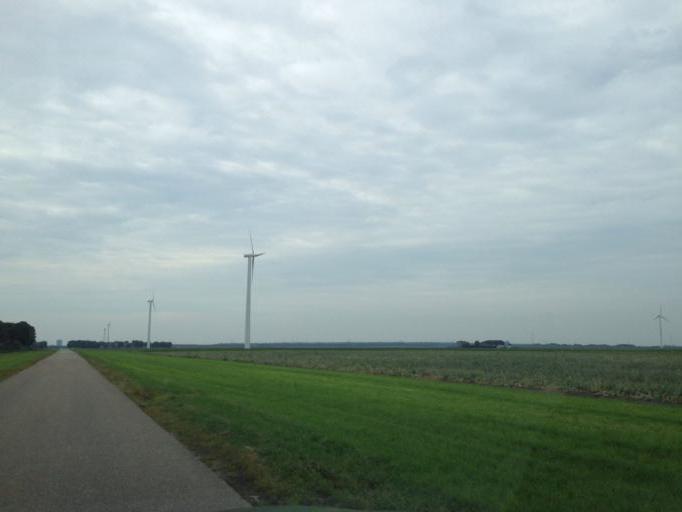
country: NL
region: Utrecht
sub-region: Gemeente Bunschoten
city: Spakenburg
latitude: 52.3649
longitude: 5.3516
